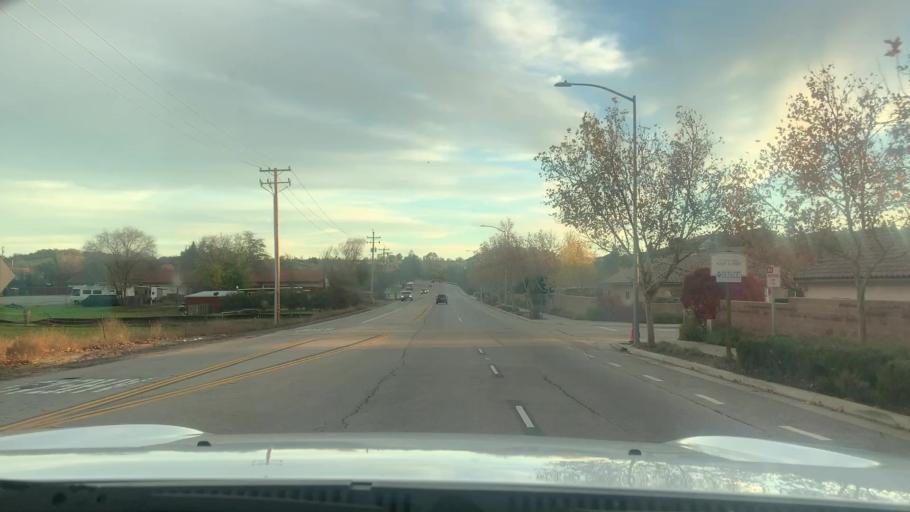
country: US
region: California
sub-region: San Luis Obispo County
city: Paso Robles
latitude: 35.6390
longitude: -120.6582
